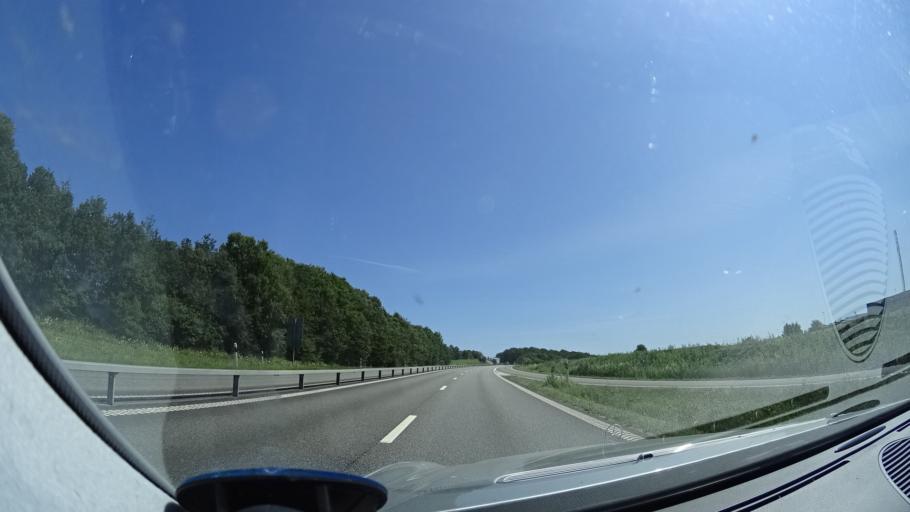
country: SE
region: Skane
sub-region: Horby Kommun
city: Hoerby
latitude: 55.8658
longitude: 13.6650
